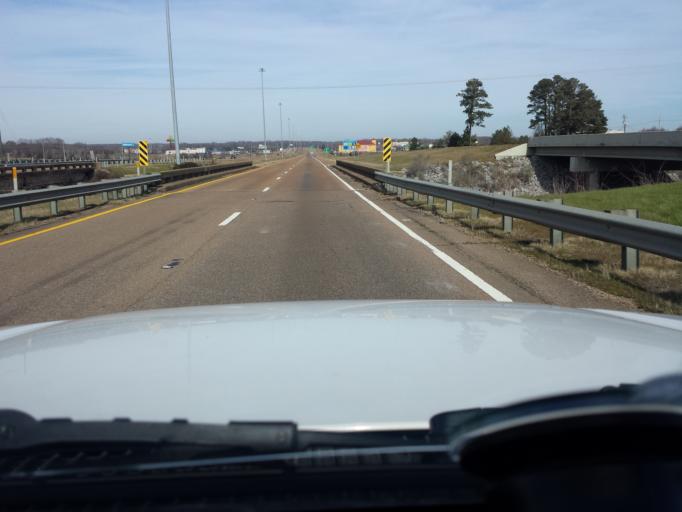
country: US
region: Mississippi
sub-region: Madison County
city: Canton
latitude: 32.5929
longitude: -90.0692
